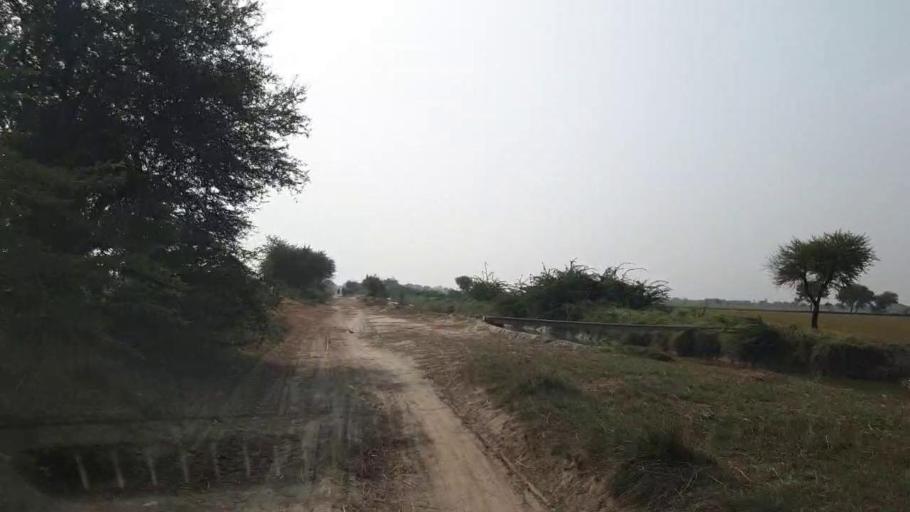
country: PK
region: Sindh
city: Kario
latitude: 24.7648
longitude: 68.5637
